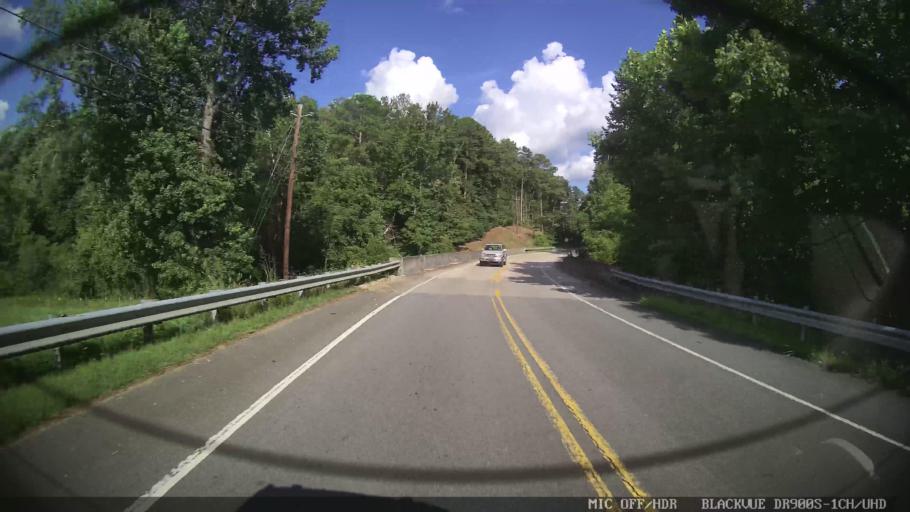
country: US
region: Georgia
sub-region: Floyd County
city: Lindale
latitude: 34.1990
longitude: -85.0821
